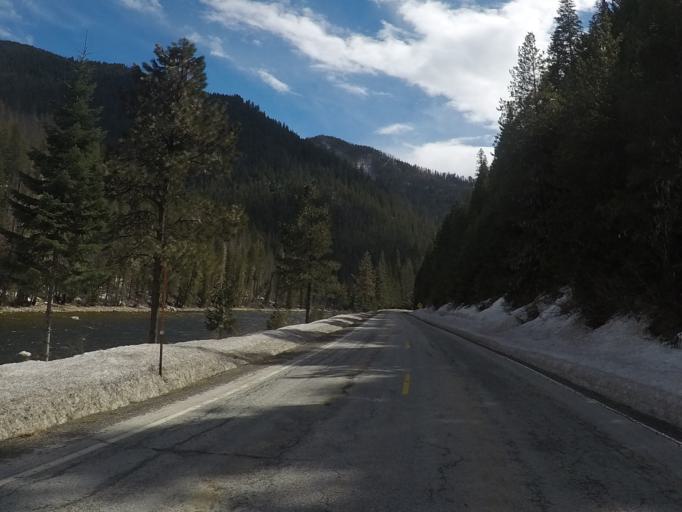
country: US
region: Montana
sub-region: Mineral County
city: Superior
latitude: 46.4807
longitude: -114.8770
